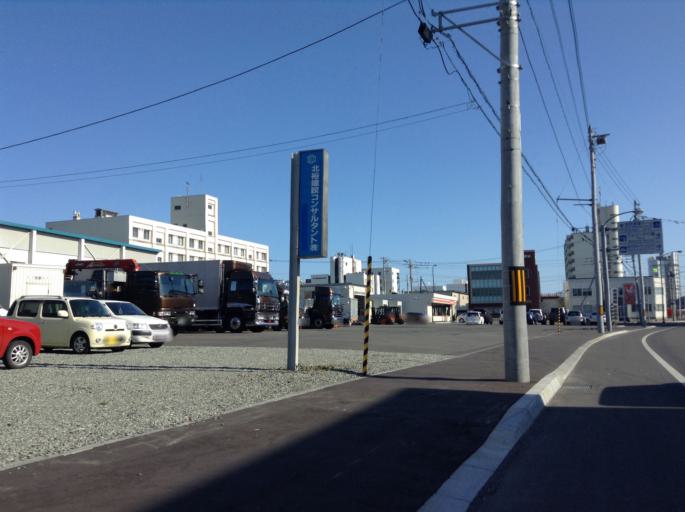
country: JP
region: Hokkaido
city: Wakkanai
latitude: 45.4136
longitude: 141.6774
